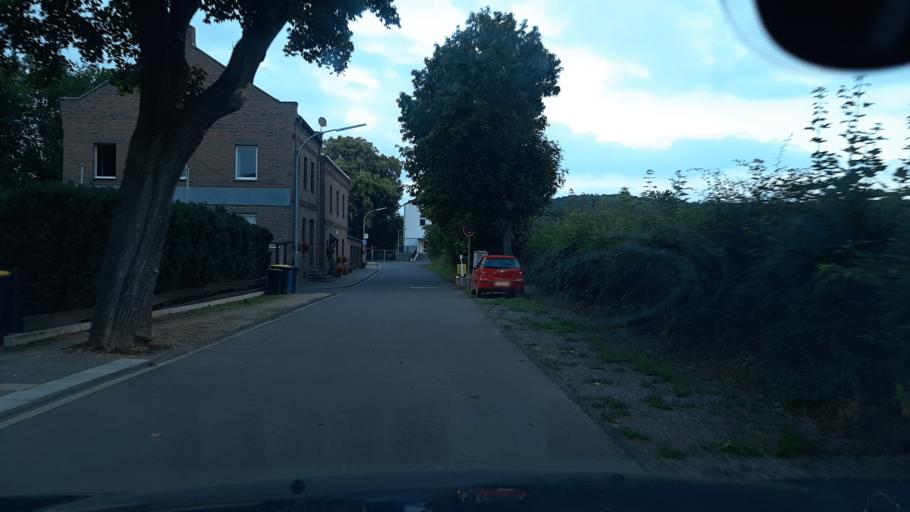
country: DE
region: North Rhine-Westphalia
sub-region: Regierungsbezirk Koln
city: Mechernich
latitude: 50.6219
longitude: 6.7121
